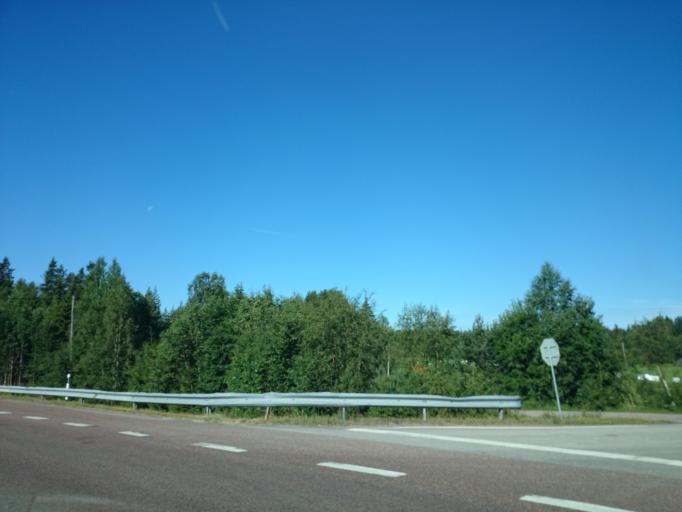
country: SE
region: Gaevleborg
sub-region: Hudiksvalls Kommun
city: Hudiksvall
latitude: 61.8041
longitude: 17.1769
